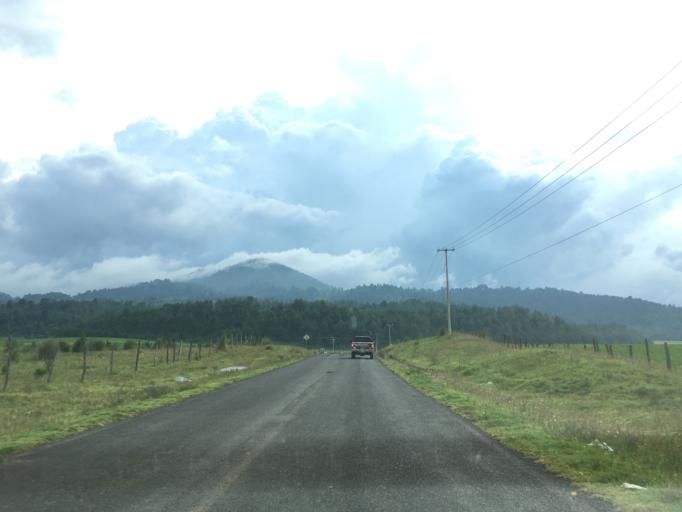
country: MX
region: Michoacan
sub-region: Nahuatzen
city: Sevina
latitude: 19.6148
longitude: -101.8566
